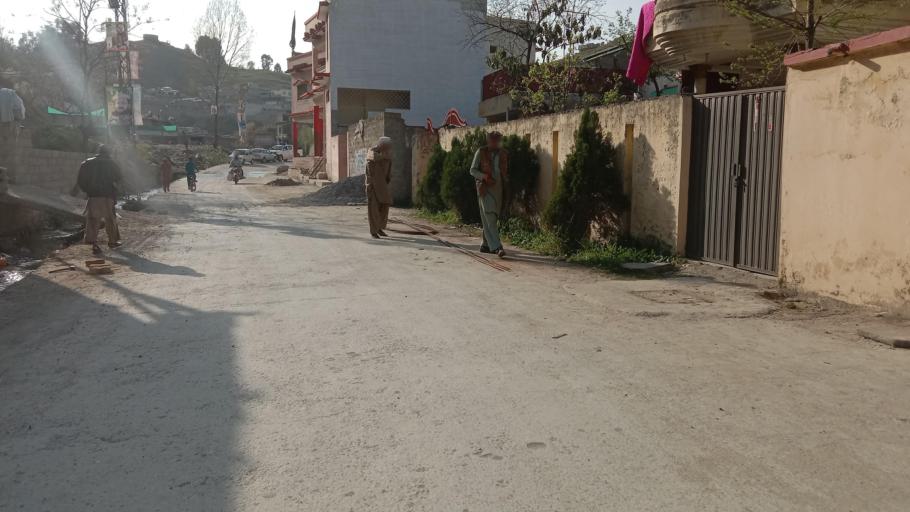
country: PK
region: Khyber Pakhtunkhwa
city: Abbottabad
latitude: 34.2031
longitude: 73.2228
